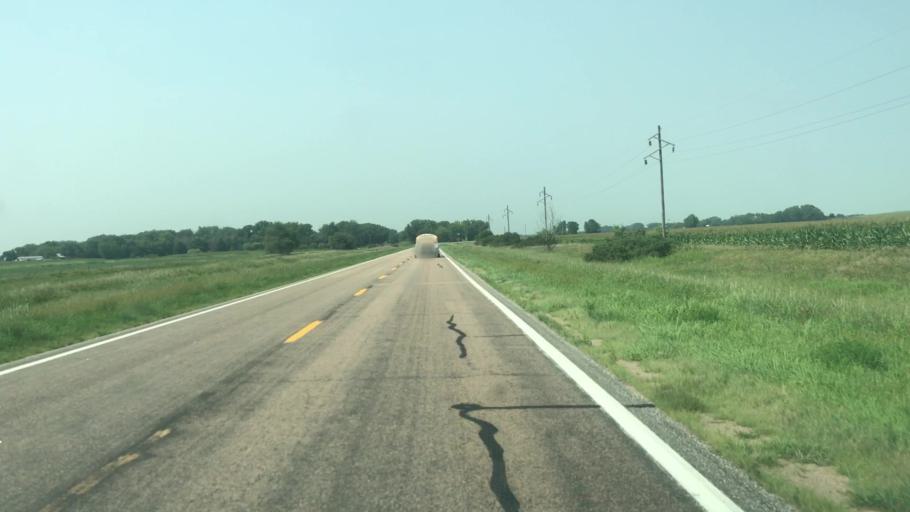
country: US
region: Nebraska
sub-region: Sherman County
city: Loup City
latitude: 41.2304
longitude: -98.9344
